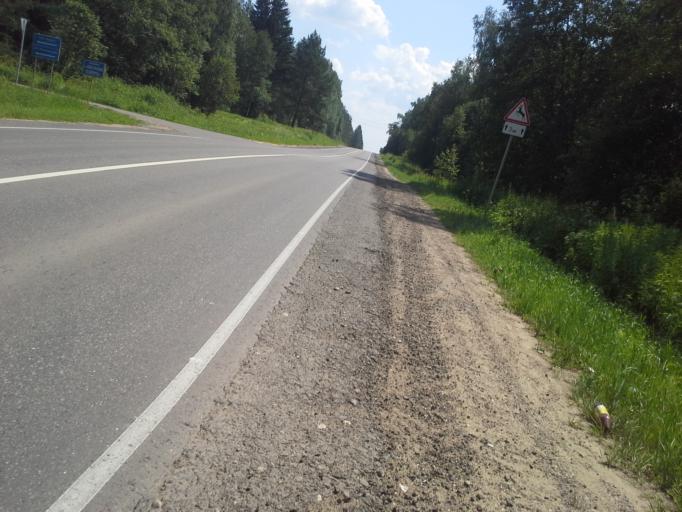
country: RU
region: Moskovskaya
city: Naro-Fominsk
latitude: 55.4629
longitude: 36.6889
